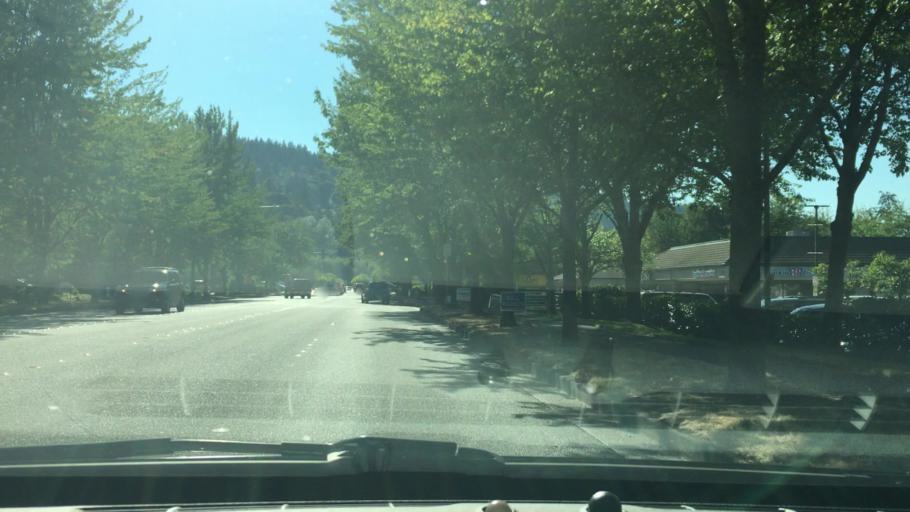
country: US
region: Washington
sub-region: King County
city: Issaquah
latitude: 47.5458
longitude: -122.0603
